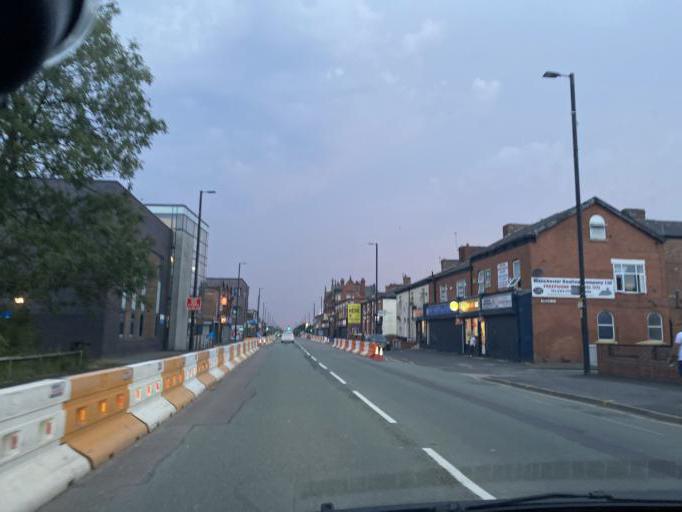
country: GB
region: England
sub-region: Borough of Tameside
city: Droylsden
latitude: 53.4728
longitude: -2.1604
